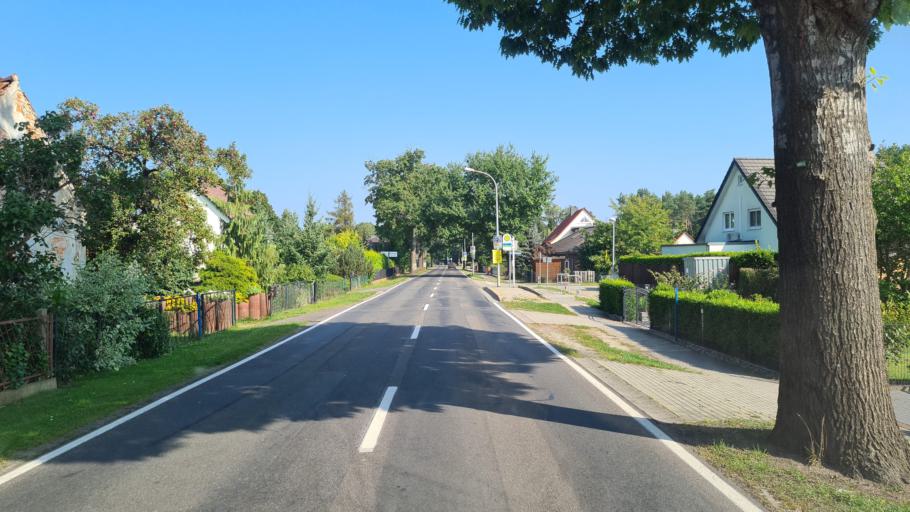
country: DE
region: Brandenburg
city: Kolkwitz
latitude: 51.7425
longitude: 14.2603
